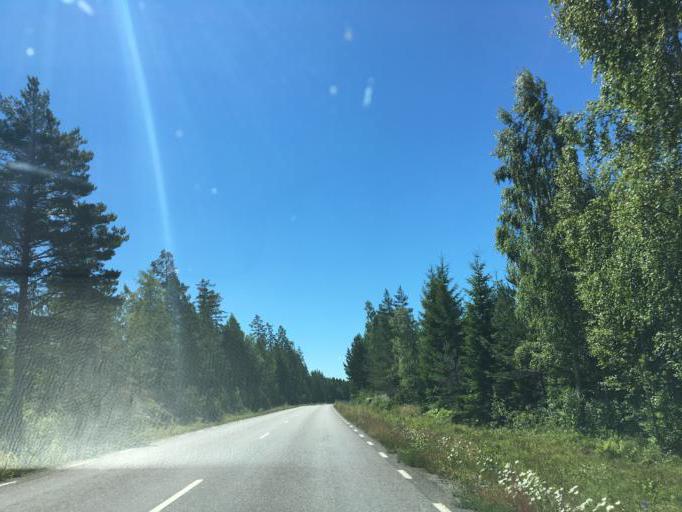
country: SE
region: OErebro
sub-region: Laxa Kommun
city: Laxa
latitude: 58.8489
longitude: 14.5486
